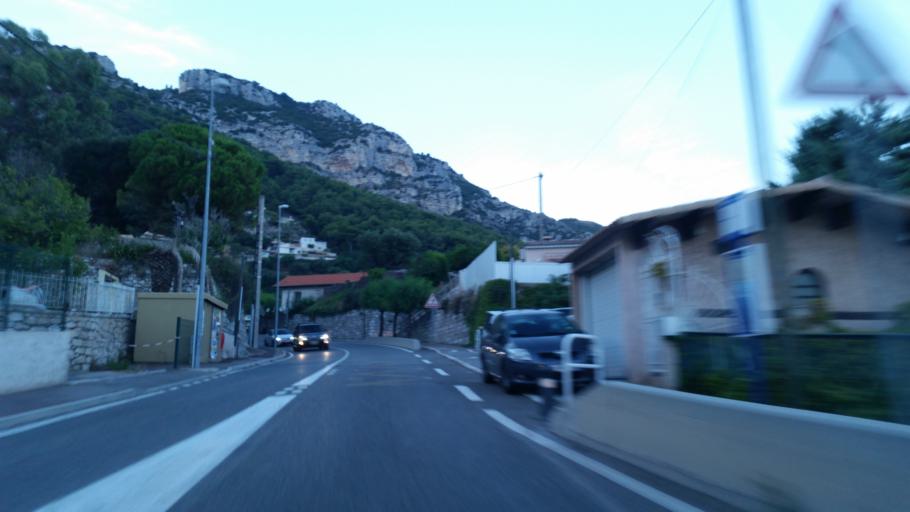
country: MC
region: Commune de Monaco
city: Saint-Roman
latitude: 43.7496
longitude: 7.4263
